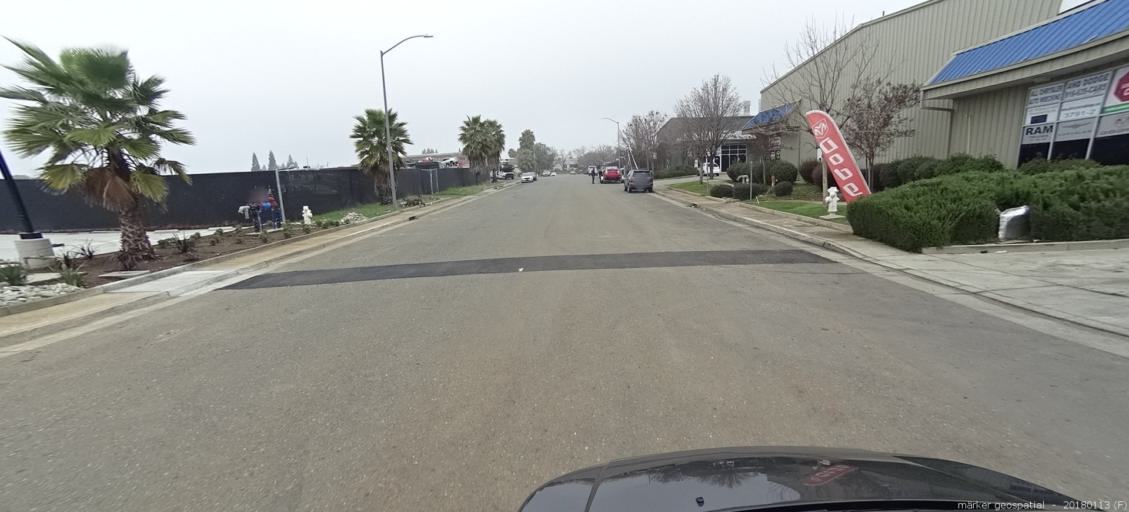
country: US
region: California
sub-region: Sacramento County
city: Rancho Cordova
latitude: 38.5652
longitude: -121.2524
